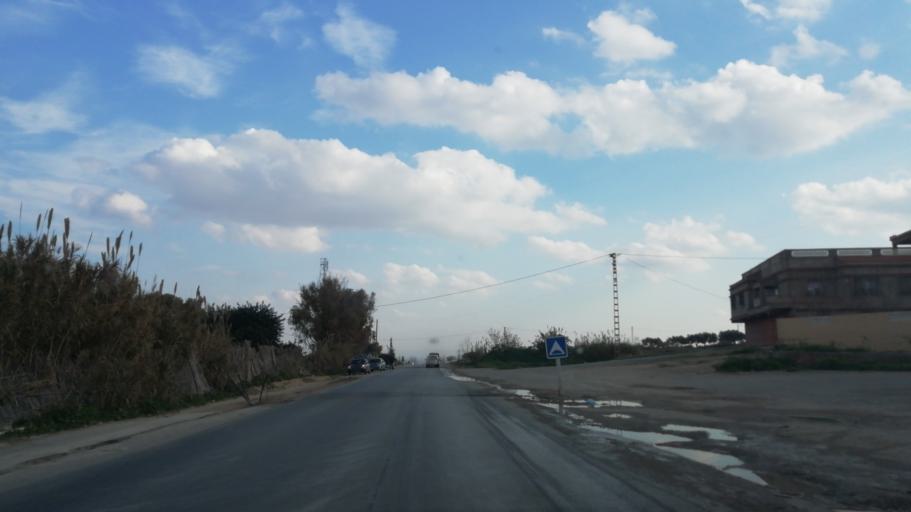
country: DZ
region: Relizane
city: Relizane
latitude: 35.9110
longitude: 0.5047
